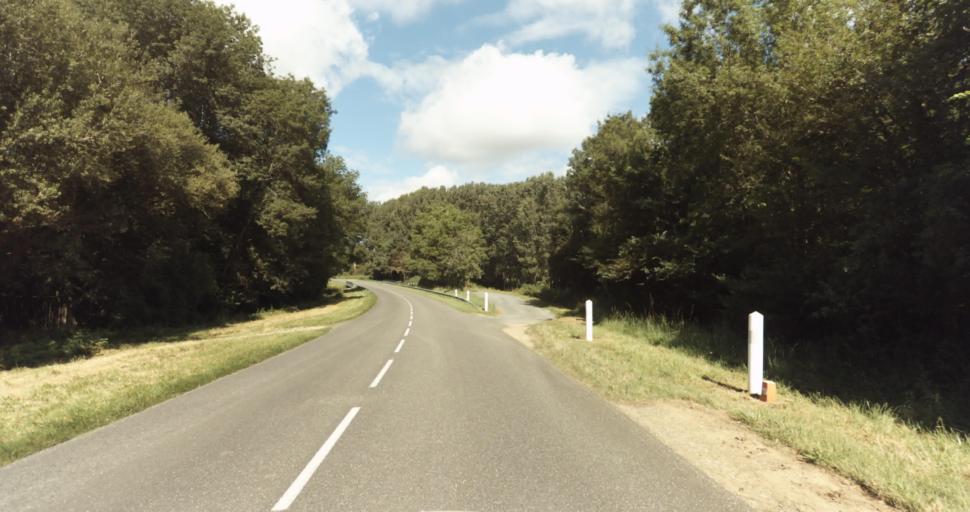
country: FR
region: Aquitaine
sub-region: Departement de la Gironde
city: Bazas
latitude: 44.4429
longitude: -0.1655
